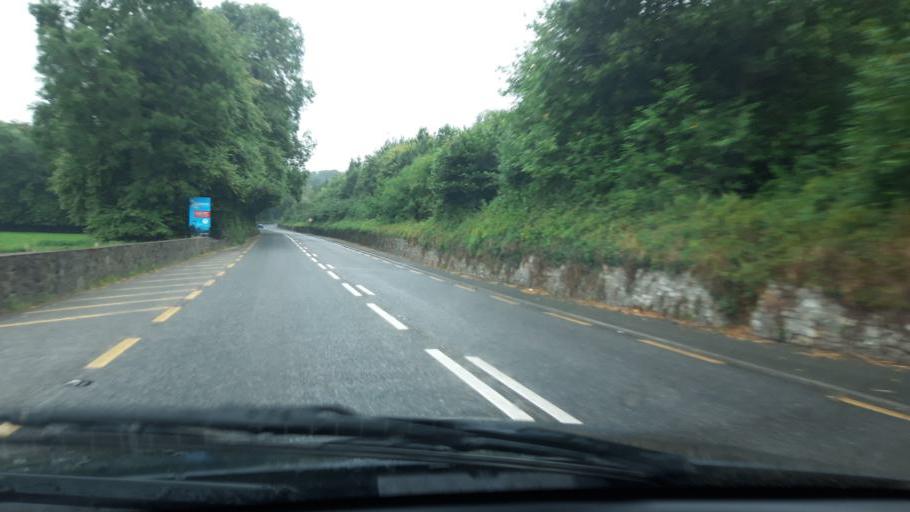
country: IE
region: Munster
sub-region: County Cork
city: Youghal
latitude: 52.1457
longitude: -7.9084
